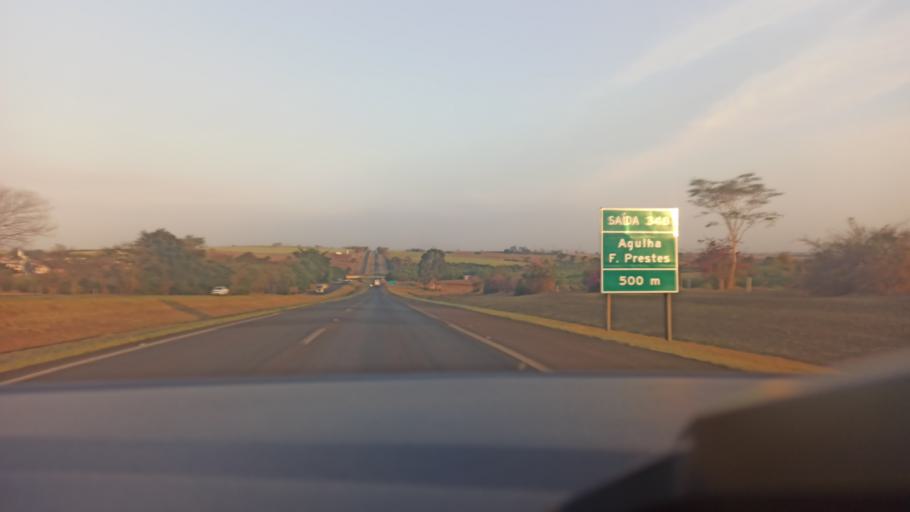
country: BR
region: Sao Paulo
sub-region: Santa Adelia
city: Santa Adelia
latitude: -21.3672
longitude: -48.7551
